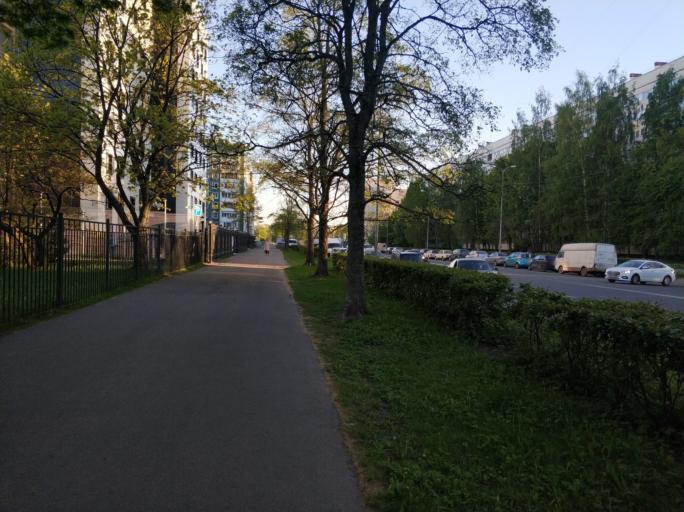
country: RU
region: St.-Petersburg
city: Grazhdanka
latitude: 60.0359
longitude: 30.3814
